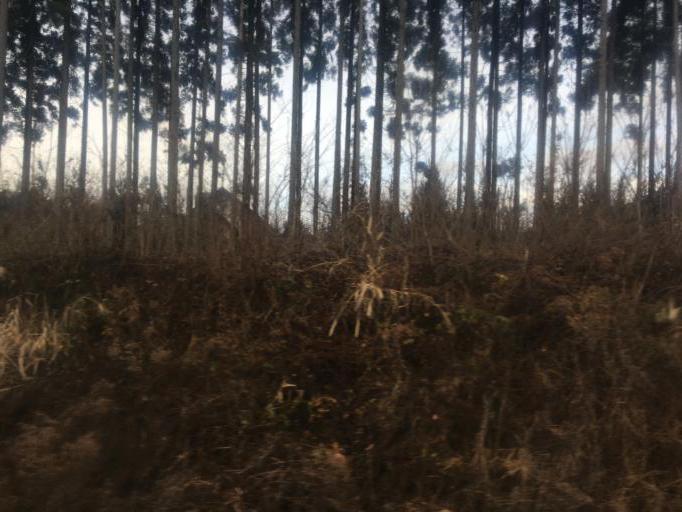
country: JP
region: Akita
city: Odate
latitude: 40.3093
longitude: 140.5726
